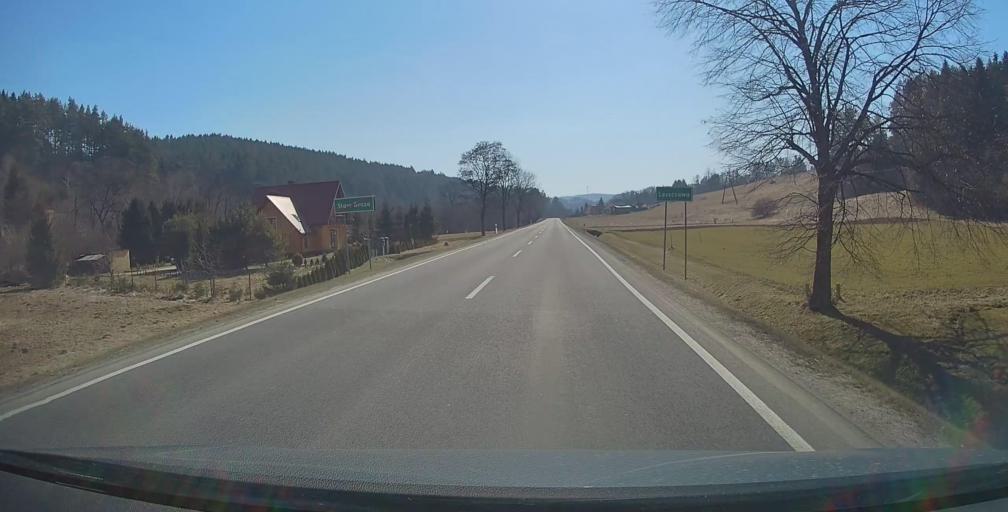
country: PL
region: Subcarpathian Voivodeship
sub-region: Powiat przemyski
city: Bircza
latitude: 49.6841
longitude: 22.4388
